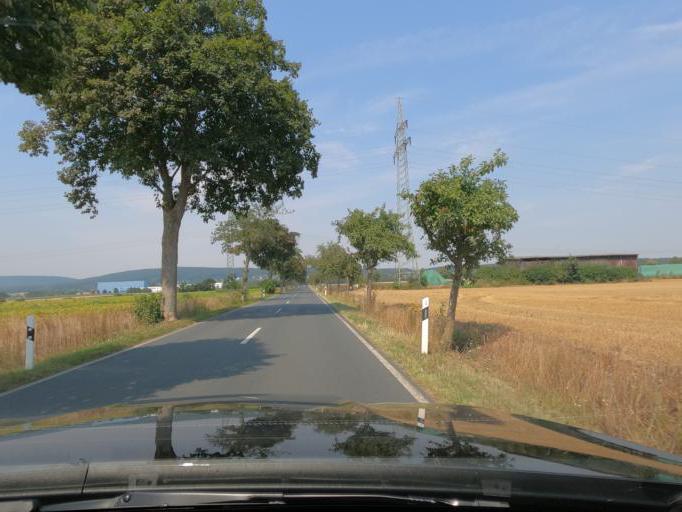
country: DE
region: Lower Saxony
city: Springe
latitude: 52.2025
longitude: 9.6331
